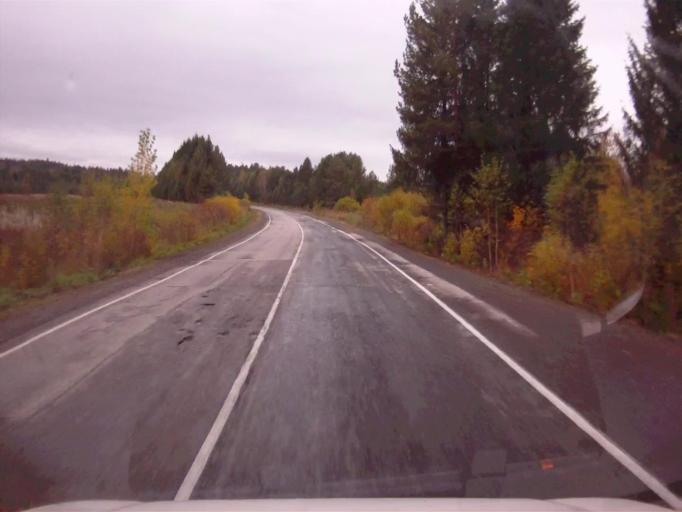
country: RU
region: Chelyabinsk
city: Nyazepetrovsk
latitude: 56.0671
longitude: 59.6972
